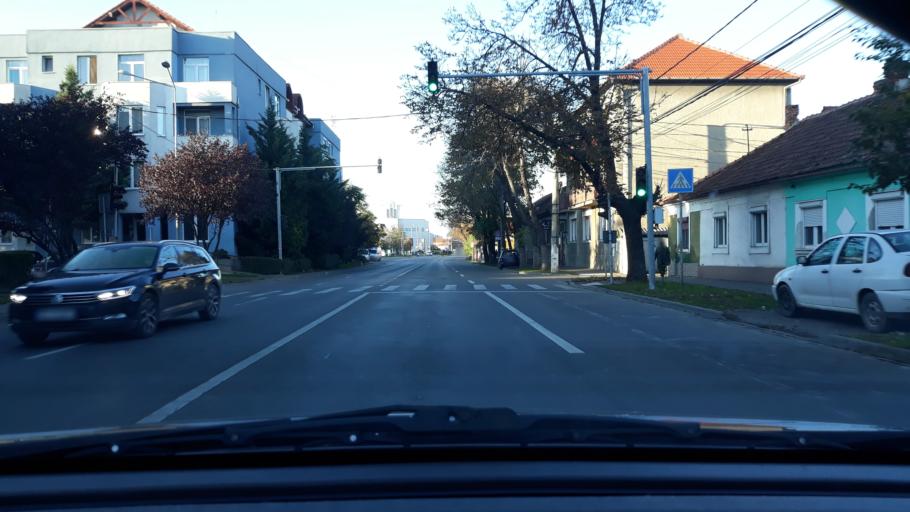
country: RO
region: Bihor
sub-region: Comuna Biharea
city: Oradea
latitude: 47.0532
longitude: 21.9187
